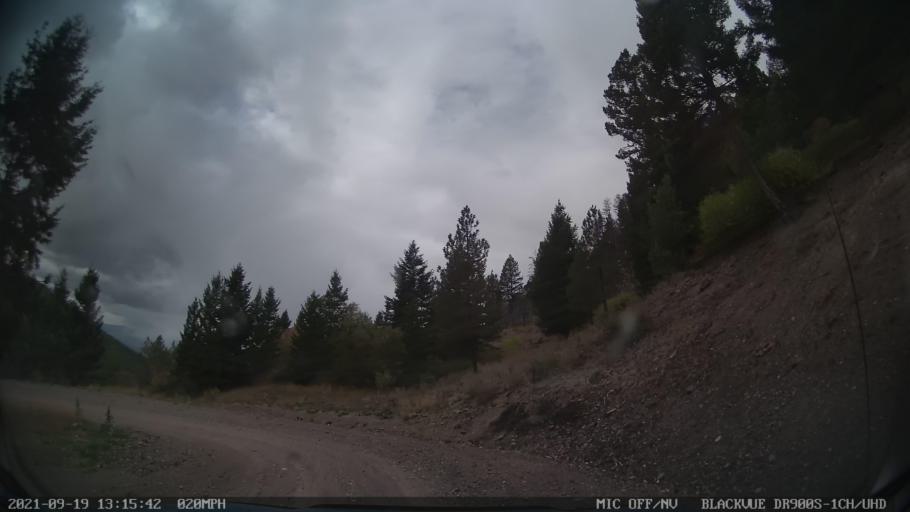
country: US
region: Montana
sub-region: Missoula County
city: Seeley Lake
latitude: 47.1800
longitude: -113.3715
